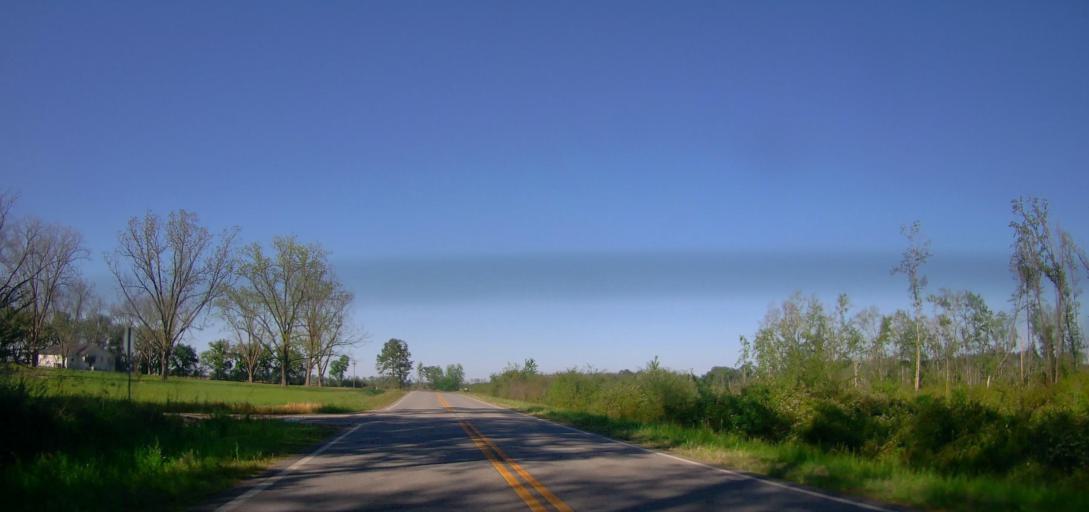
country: US
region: Georgia
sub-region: Wilcox County
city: Rochelle
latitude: 31.9084
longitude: -83.4810
